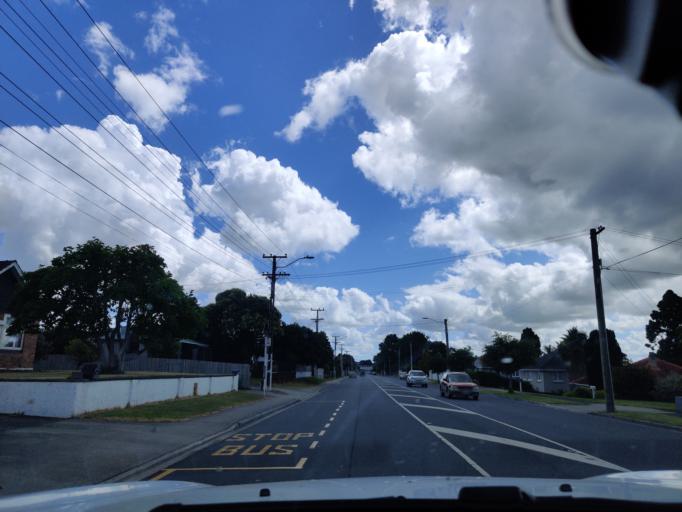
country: NZ
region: Auckland
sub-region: Auckland
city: Papakura
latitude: -37.0572
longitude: 174.9555
